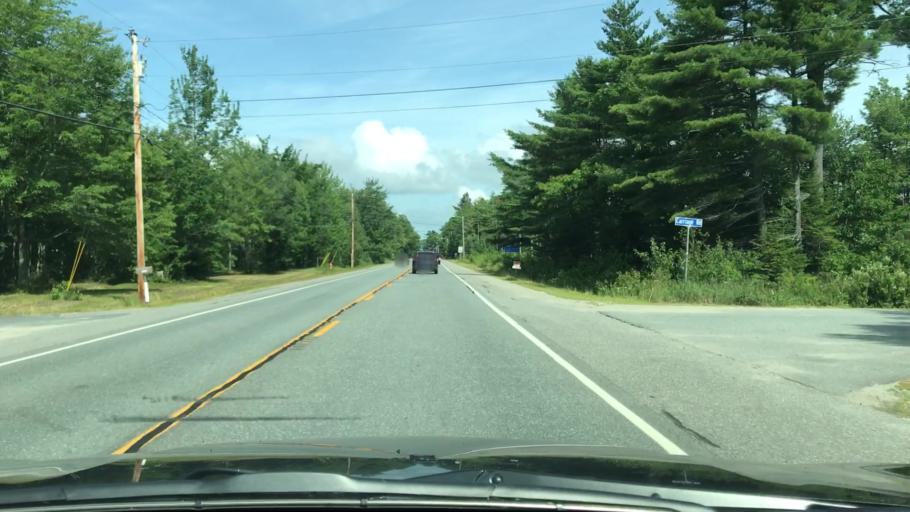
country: US
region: Maine
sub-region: Hancock County
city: Ellsworth
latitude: 44.5392
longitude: -68.4452
